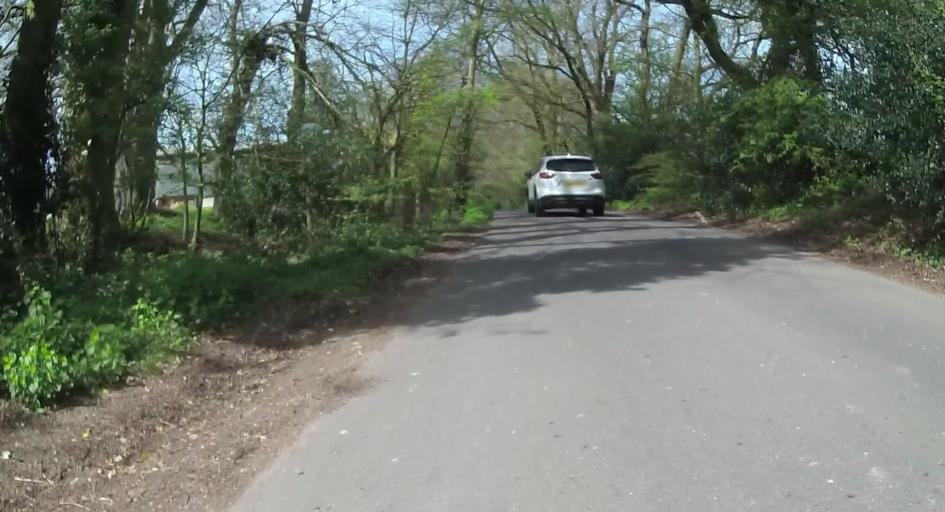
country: GB
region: England
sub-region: Hampshire
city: Chandlers Ford
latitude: 51.0602
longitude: -1.3735
